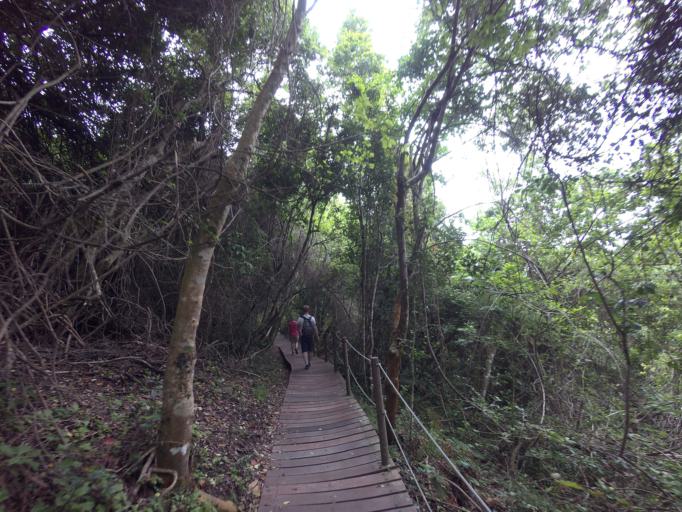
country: ZA
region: Eastern Cape
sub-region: Cacadu District Municipality
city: Kareedouw
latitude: -34.0216
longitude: 23.8974
